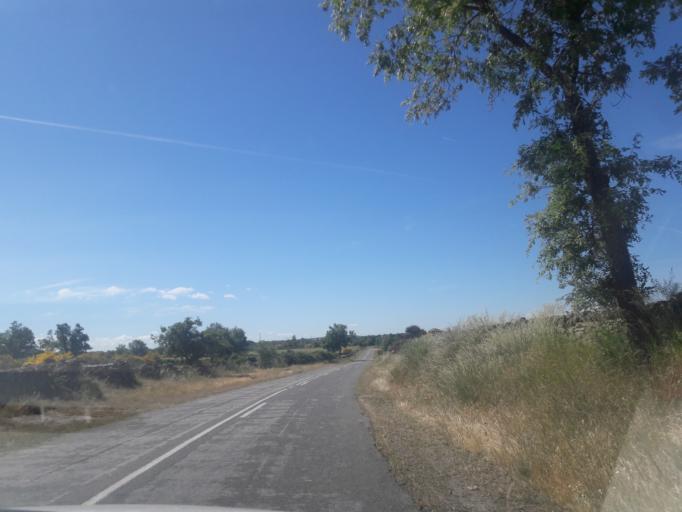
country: ES
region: Castille and Leon
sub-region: Provincia de Salamanca
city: Lumbrales
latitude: 40.9552
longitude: -6.7196
